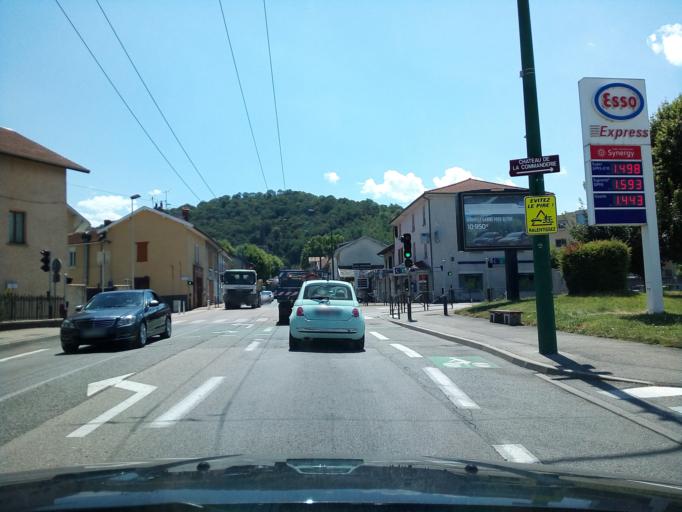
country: FR
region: Rhone-Alpes
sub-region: Departement de l'Isere
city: Eybens
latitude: 45.1502
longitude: 5.7500
